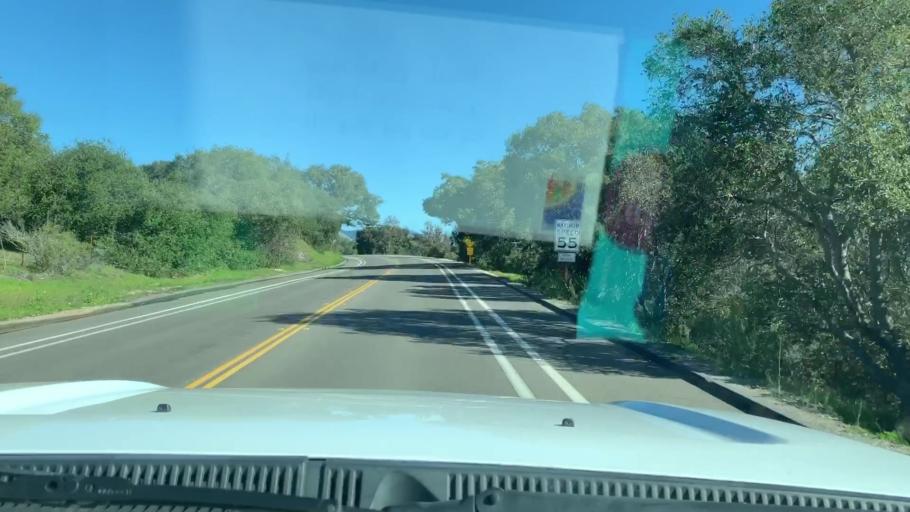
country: US
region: California
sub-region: San Luis Obispo County
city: Pismo Beach
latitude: 35.1786
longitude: -120.6206
